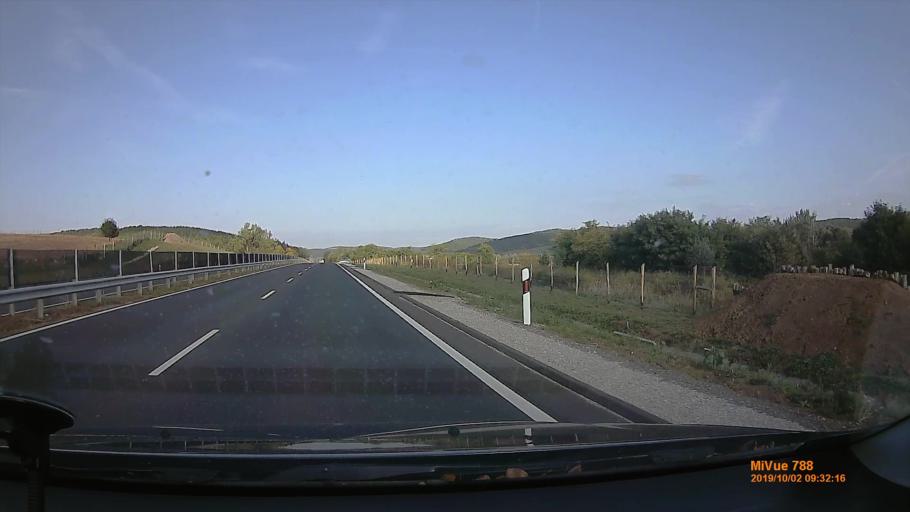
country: HU
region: Nograd
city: Kazar
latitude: 48.0285
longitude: 19.8144
